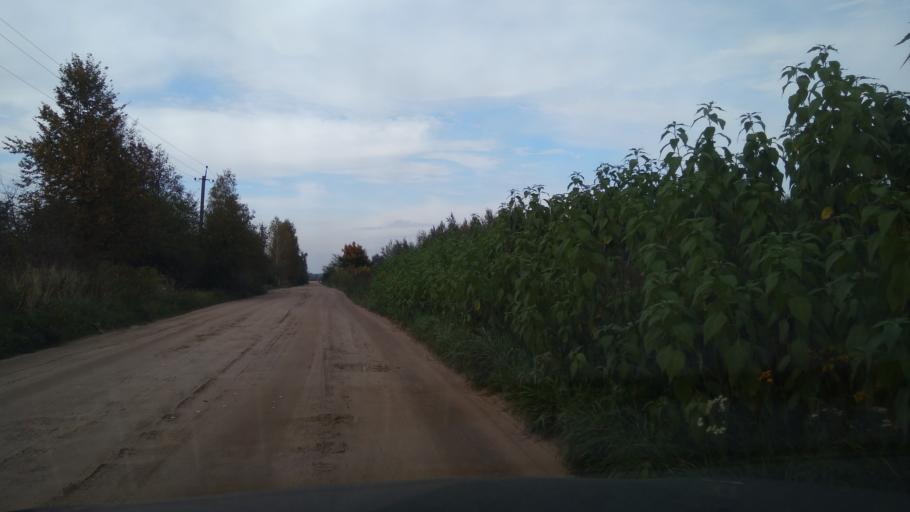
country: BY
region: Minsk
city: Rudzyensk
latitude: 53.6107
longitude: 27.8479
